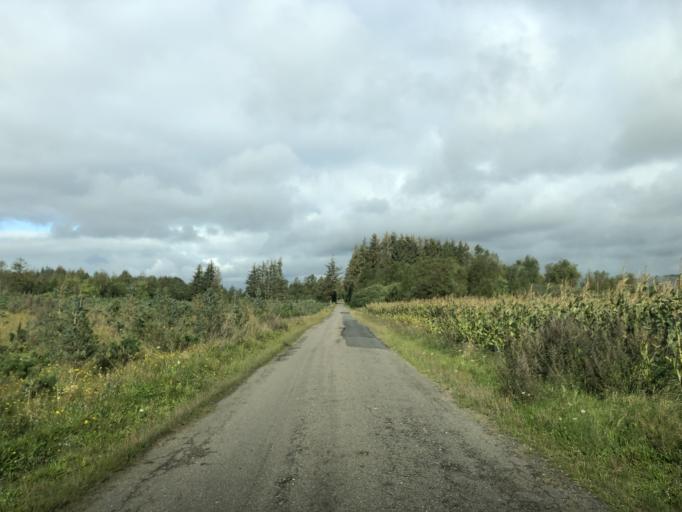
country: DK
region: Central Jutland
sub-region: Holstebro Kommune
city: Ulfborg
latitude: 56.2943
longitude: 8.4536
